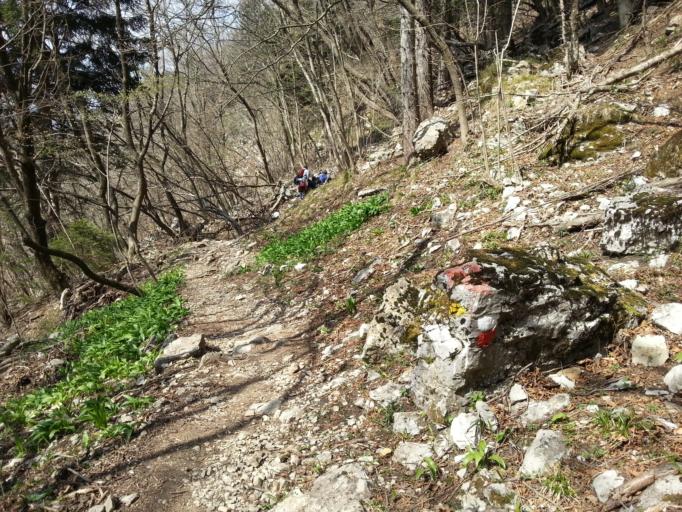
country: IT
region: Lombardy
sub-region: Provincia di Lecco
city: Suello
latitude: 45.8473
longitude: 9.3146
